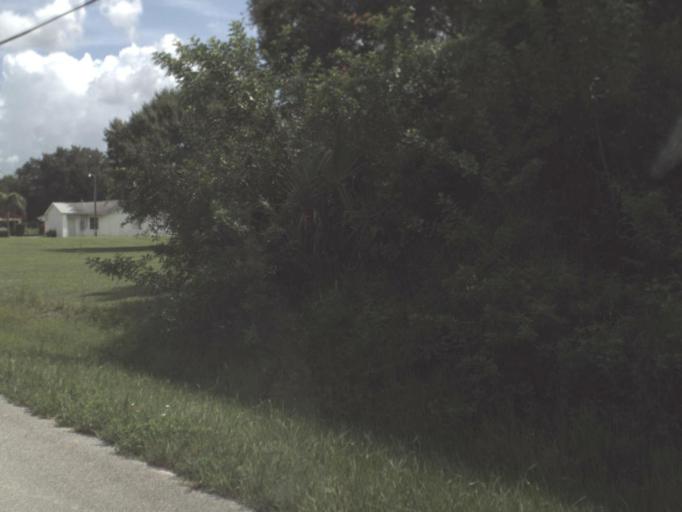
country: US
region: Florida
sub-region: DeSoto County
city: Nocatee
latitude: 27.1524
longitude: -81.8886
